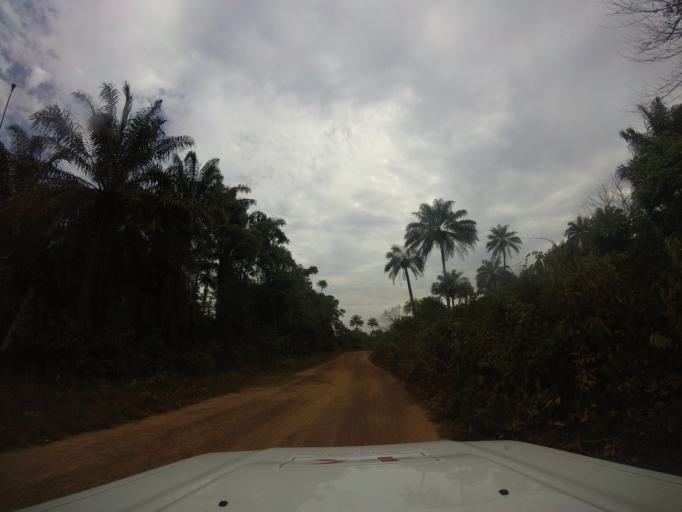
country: SL
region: Southern Province
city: Zimmi
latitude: 7.0363
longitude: -11.2831
